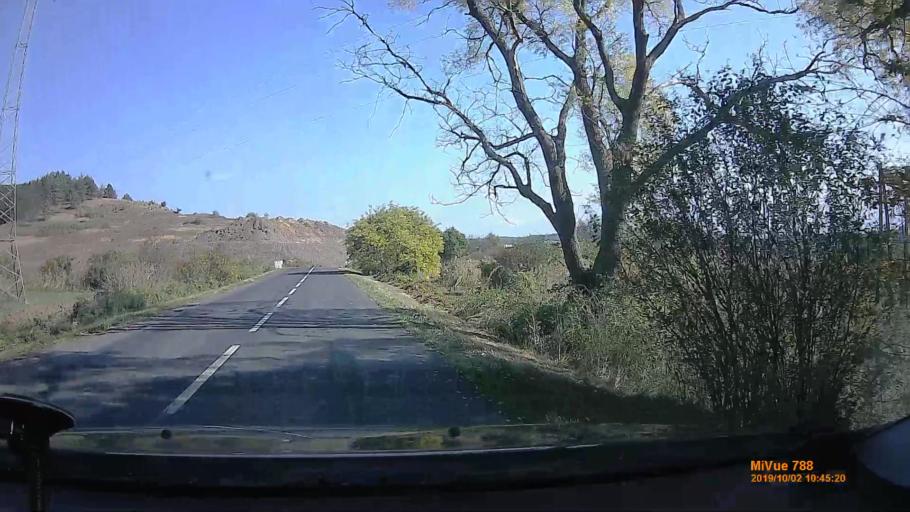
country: HU
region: Nograd
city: Batonyterenye
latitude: 47.9924
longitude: 19.8123
